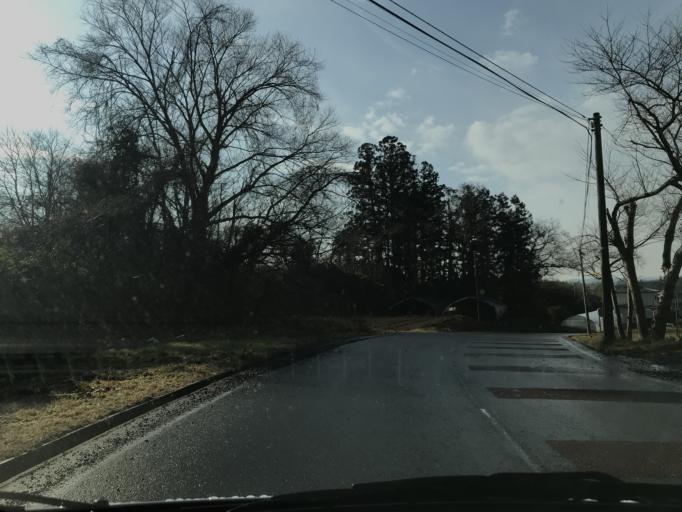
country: JP
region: Iwate
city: Ichinoseki
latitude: 38.7550
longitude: 141.1663
